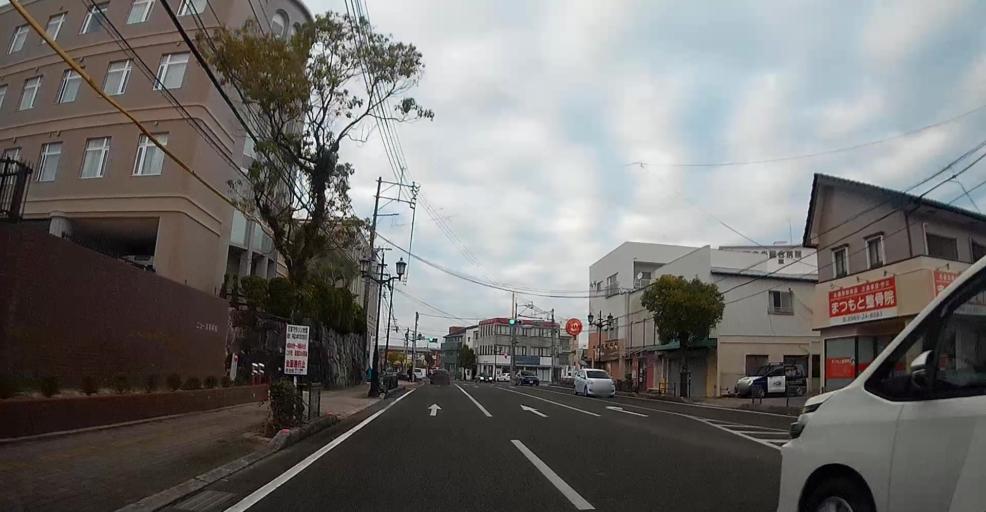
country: JP
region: Kumamoto
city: Hondo
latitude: 32.4491
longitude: 130.1994
